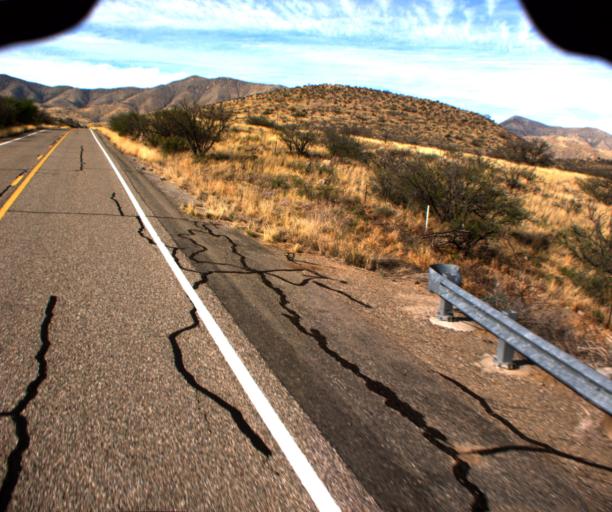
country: US
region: Arizona
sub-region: Cochise County
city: Willcox
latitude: 32.1463
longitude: -109.5650
